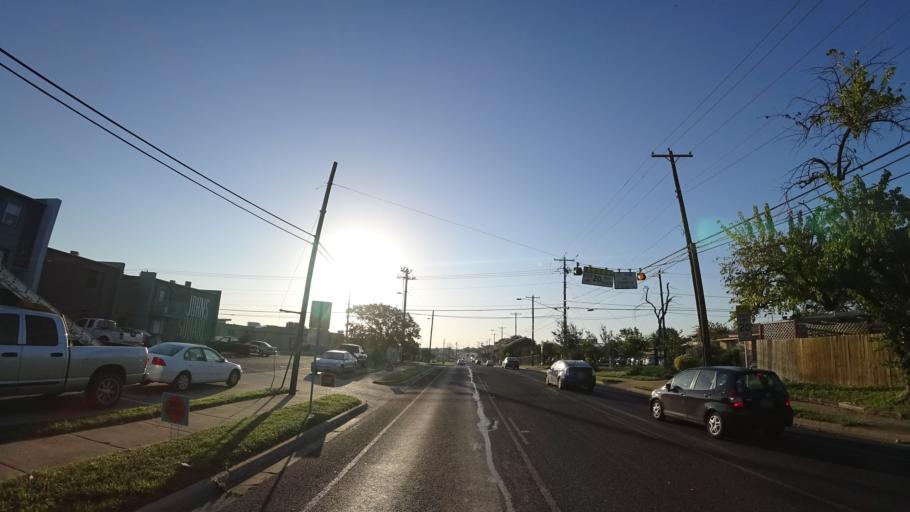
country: US
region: Texas
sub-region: Travis County
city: Austin
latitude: 30.3345
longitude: -97.7077
